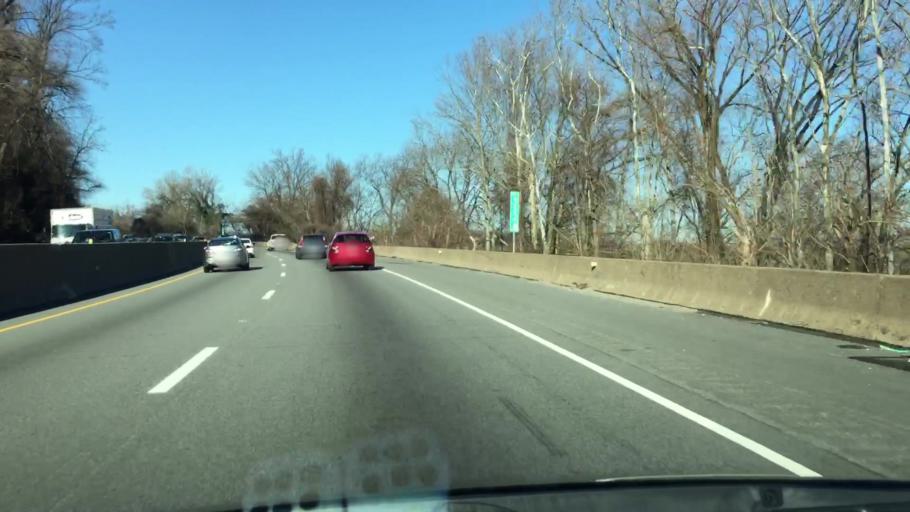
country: US
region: Pennsylvania
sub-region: Montgomery County
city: Conshohocken
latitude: 40.0699
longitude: -75.2800
